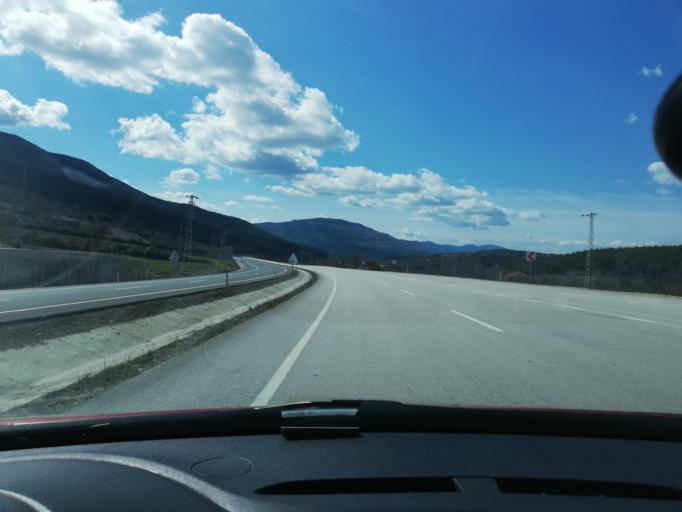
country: TR
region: Karabuk
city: Ovacik
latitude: 41.2171
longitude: 32.9771
